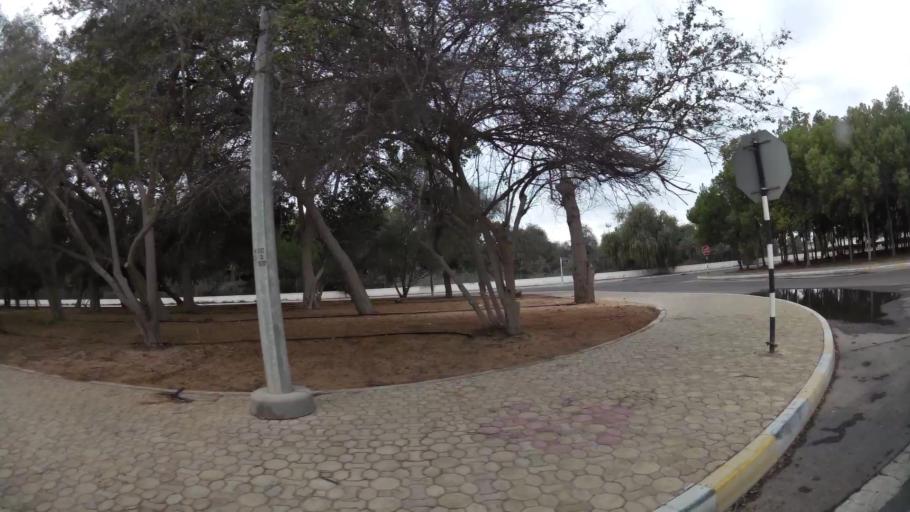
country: AE
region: Abu Dhabi
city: Abu Dhabi
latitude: 24.4309
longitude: 54.3804
